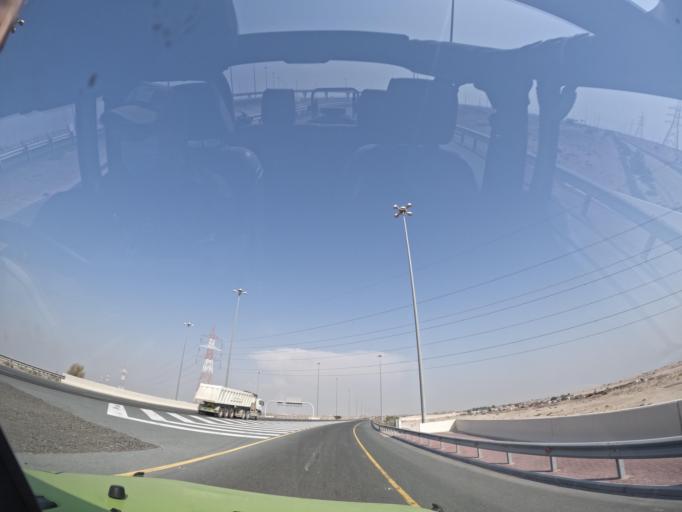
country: AE
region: Abu Dhabi
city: Abu Dhabi
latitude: 24.6780
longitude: 54.8273
